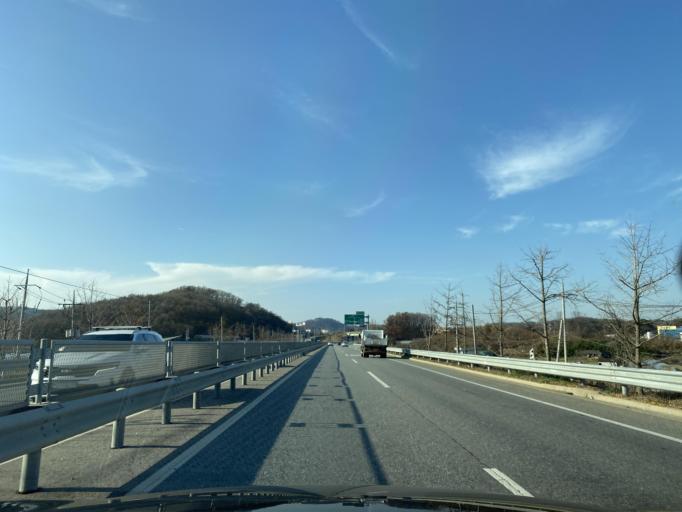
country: KR
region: Chungcheongnam-do
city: Asan
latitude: 36.7620
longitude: 126.9529
